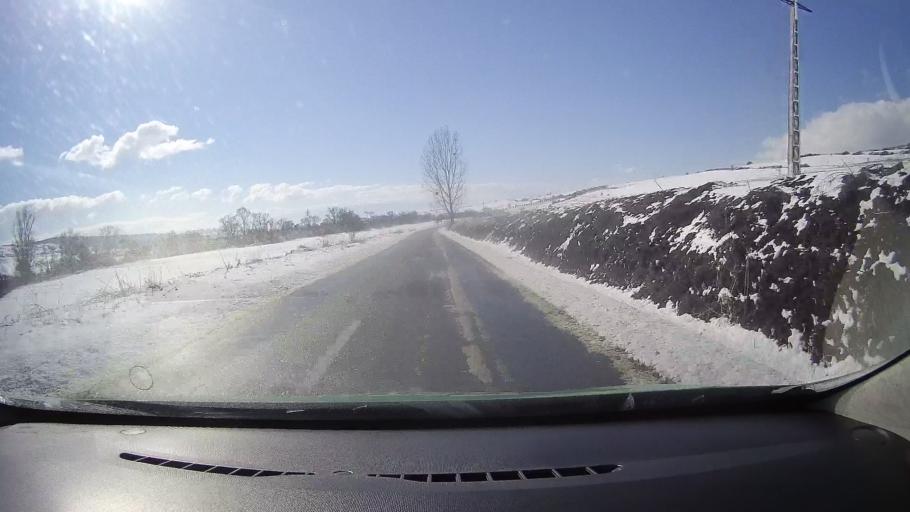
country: RO
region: Sibiu
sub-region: Comuna Vurpar
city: Vurpar
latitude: 45.8822
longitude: 24.3271
